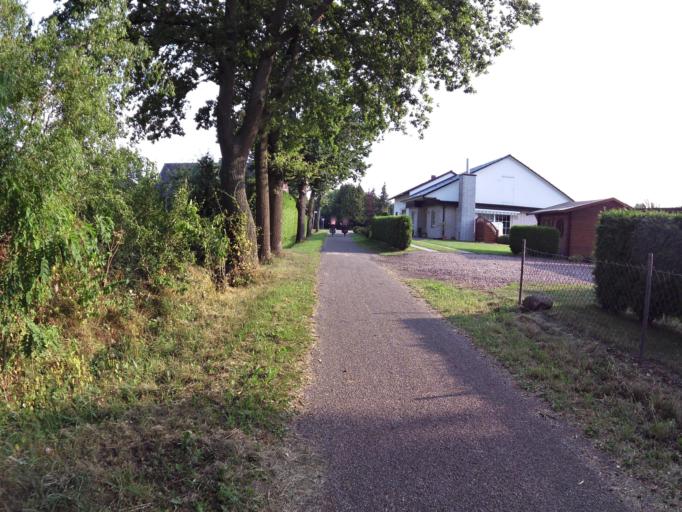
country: DE
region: North Rhine-Westphalia
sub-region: Regierungsbezirk Detmold
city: Petershagen
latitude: 52.4099
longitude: 8.9689
